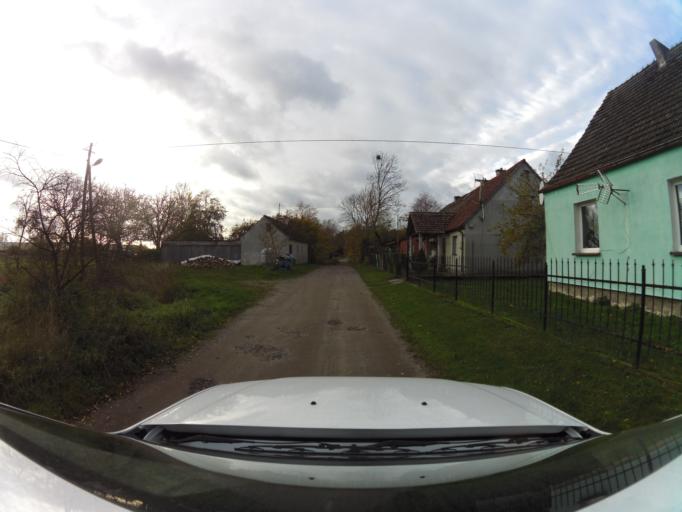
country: PL
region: West Pomeranian Voivodeship
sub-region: Powiat goleniowski
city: Nowogard
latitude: 53.6961
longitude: 15.1050
